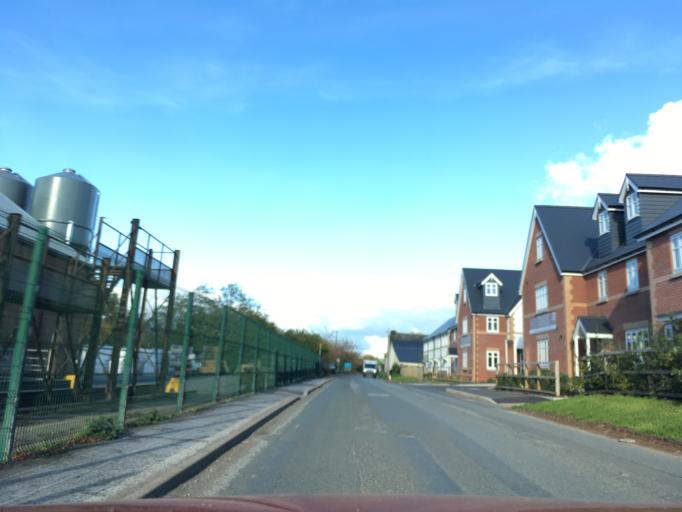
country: GB
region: Wales
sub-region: Sir Powys
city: Hay
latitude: 52.0787
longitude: -3.1234
